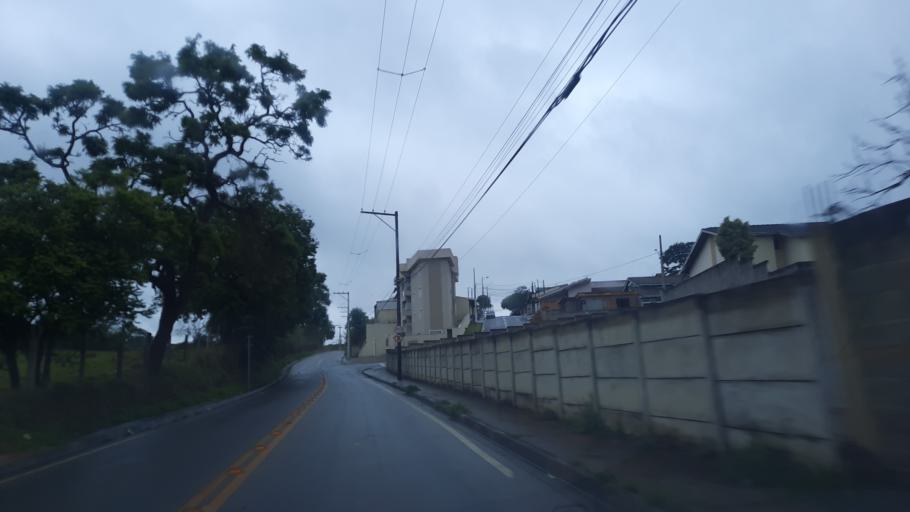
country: BR
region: Sao Paulo
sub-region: Atibaia
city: Atibaia
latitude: -23.0933
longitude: -46.5416
